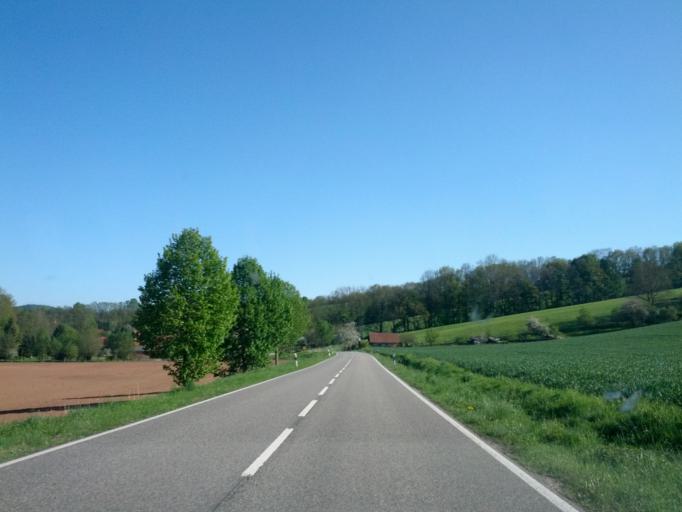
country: DE
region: Thuringia
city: Sickerode
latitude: 51.2571
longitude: 10.1152
